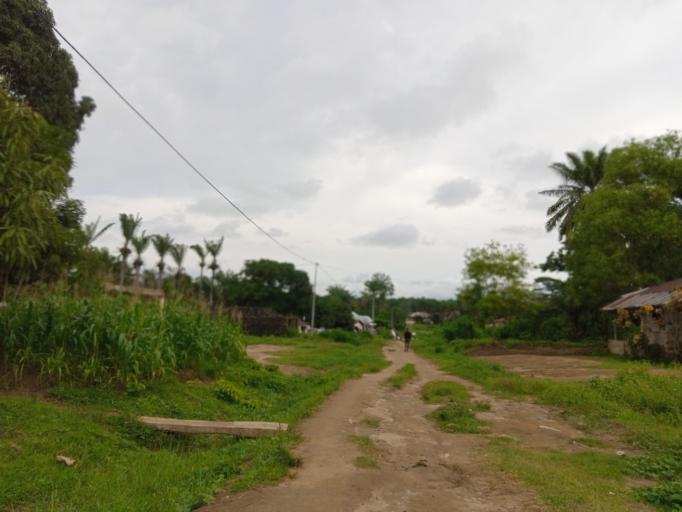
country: SL
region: Northern Province
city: Masoyila
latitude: 8.5990
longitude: -13.2018
